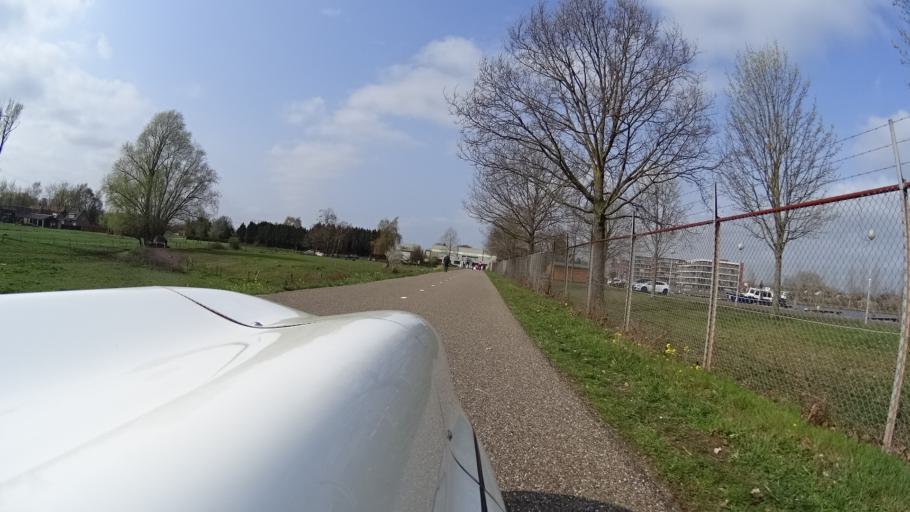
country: NL
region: North Brabant
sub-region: Gemeente Son en Breugel
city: Son
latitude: 51.5050
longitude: 5.4986
